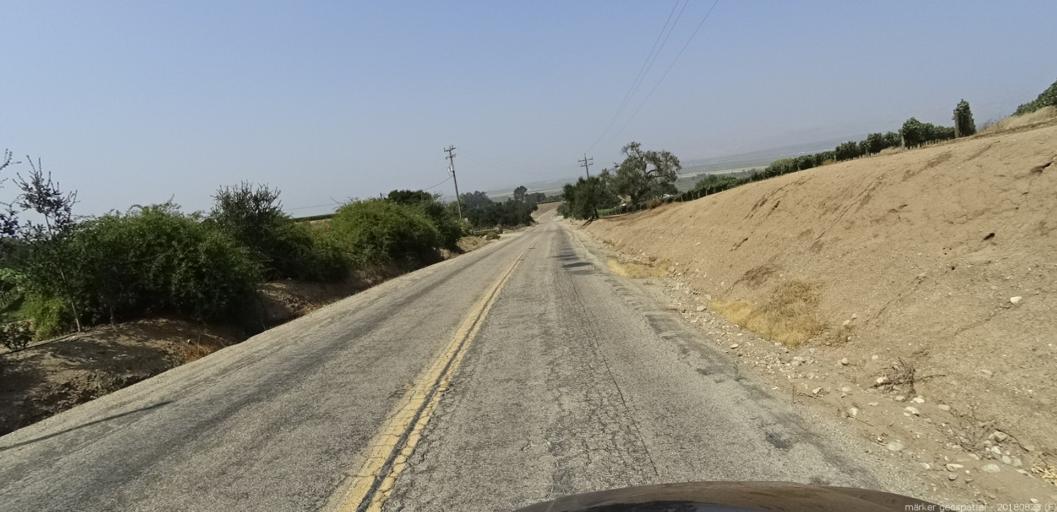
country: US
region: California
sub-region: Monterey County
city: Gonzales
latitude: 36.4392
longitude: -121.4317
